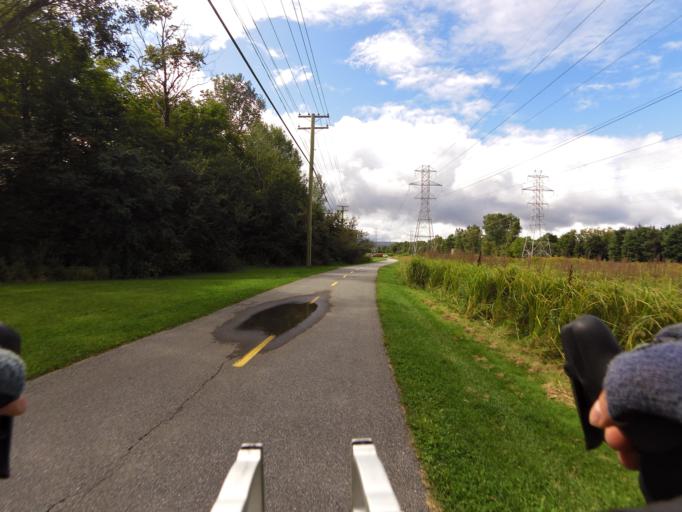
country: CA
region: Quebec
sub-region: Outaouais
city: Gatineau
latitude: 45.4979
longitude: -75.7366
